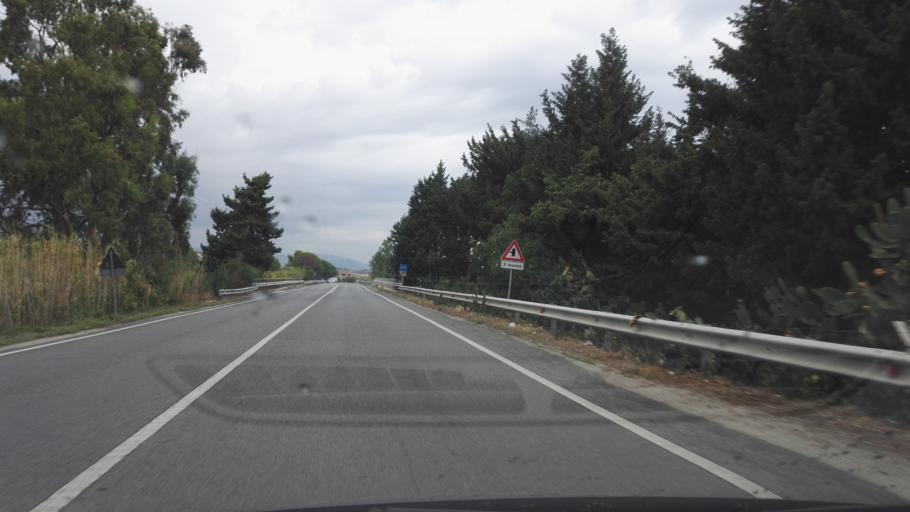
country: IT
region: Calabria
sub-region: Provincia di Catanzaro
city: Isca Marina
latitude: 38.6071
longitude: 16.5561
